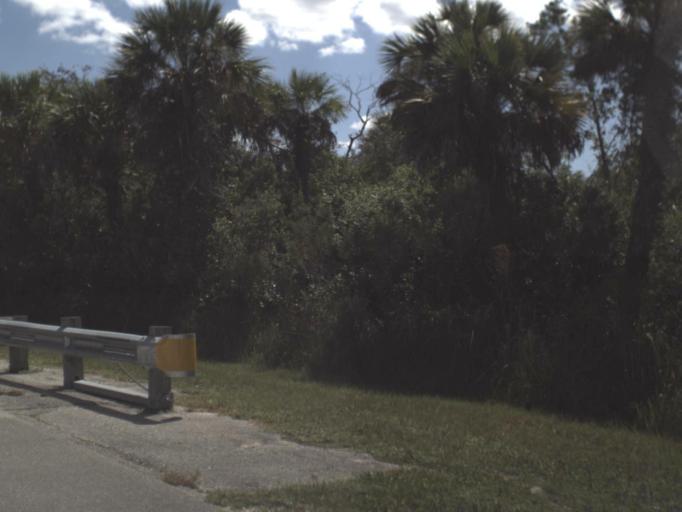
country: US
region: Florida
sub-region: Collier County
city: Marco
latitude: 25.9836
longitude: -81.5654
